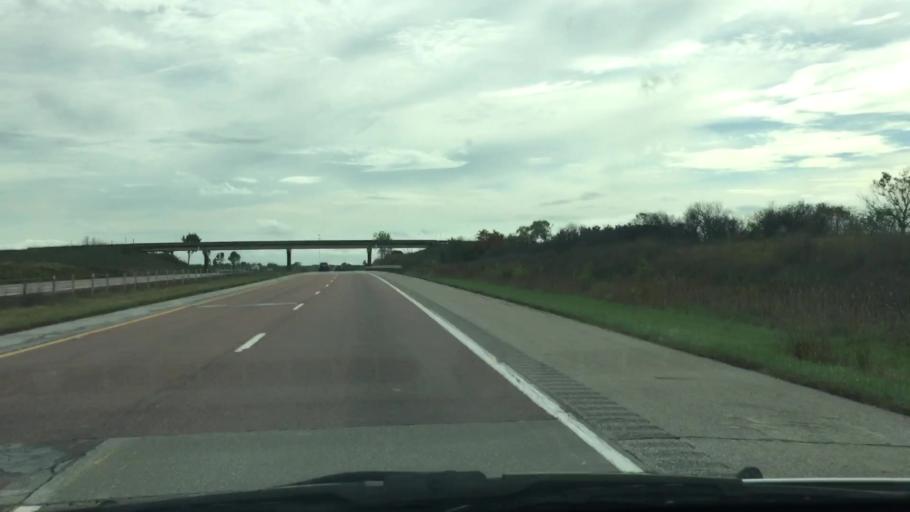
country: US
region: Iowa
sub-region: Clarke County
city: Osceola
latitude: 41.2550
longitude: -93.7810
